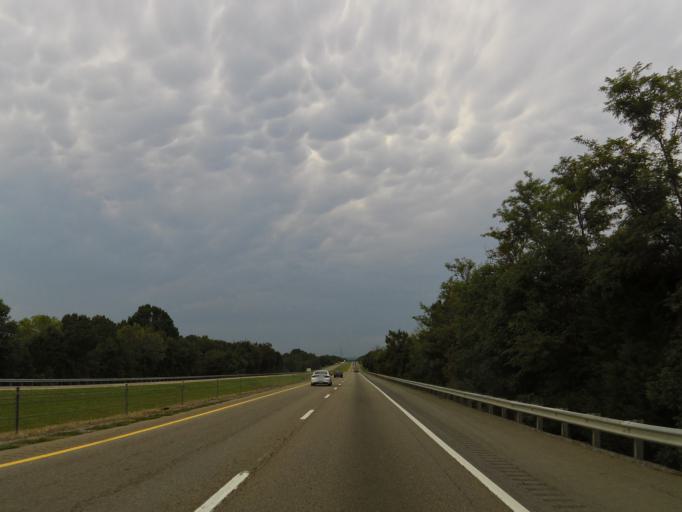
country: US
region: Tennessee
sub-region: Cocke County
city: Newport
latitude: 35.9955
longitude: -83.2859
